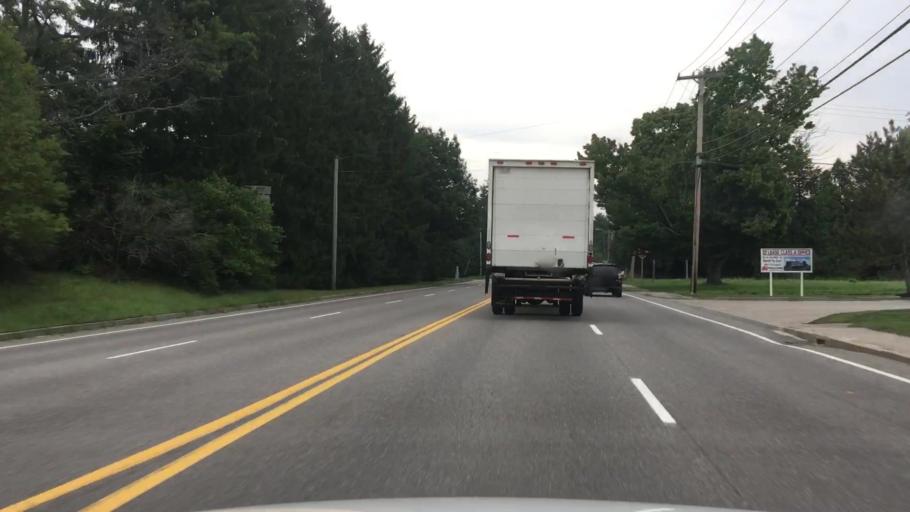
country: US
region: Maine
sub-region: Cumberland County
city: South Portland Gardens
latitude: 43.6493
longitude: -70.3251
